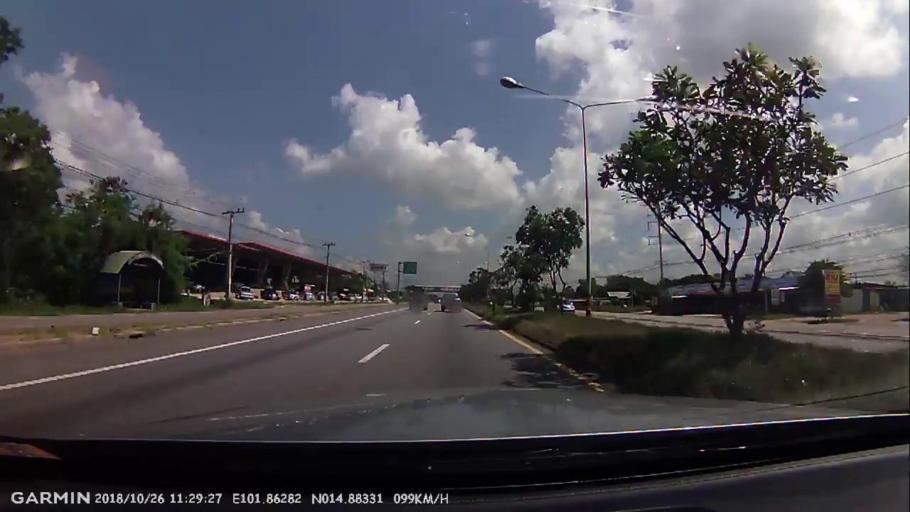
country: TH
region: Nakhon Ratchasima
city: Sung Noen
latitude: 14.8836
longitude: 101.8629
